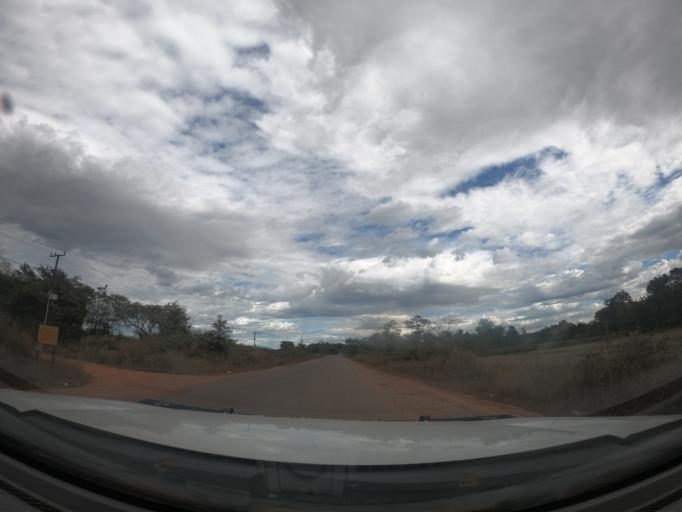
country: LA
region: Bolikhamxai
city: Muang Pakxan
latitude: 18.3777
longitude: 103.7416
